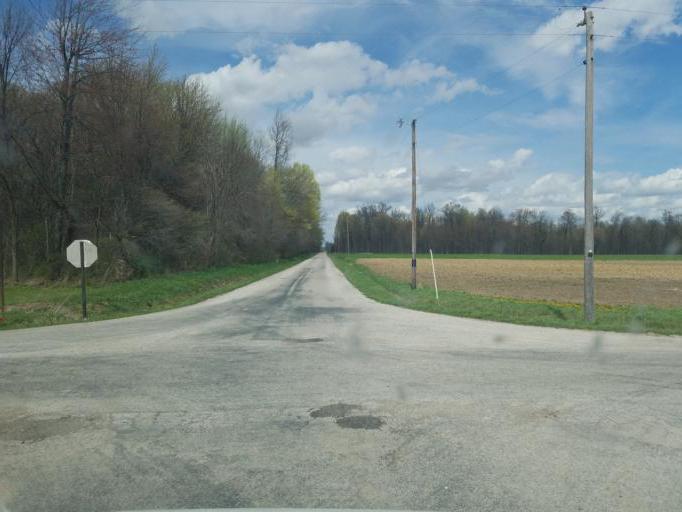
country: US
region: Ohio
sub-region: Crawford County
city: Bucyrus
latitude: 40.9214
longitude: -82.9210
